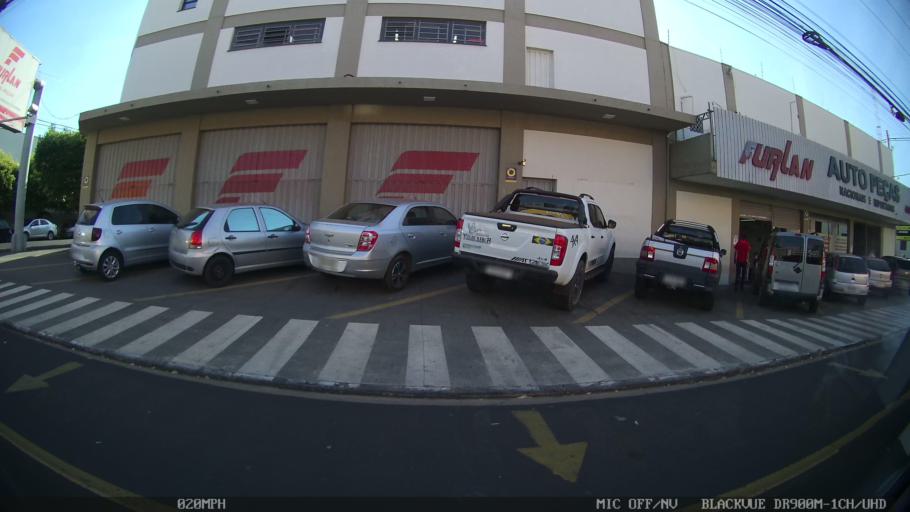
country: BR
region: Sao Paulo
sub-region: Sao Jose Do Rio Preto
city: Sao Jose do Rio Preto
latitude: -20.7899
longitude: -49.3582
